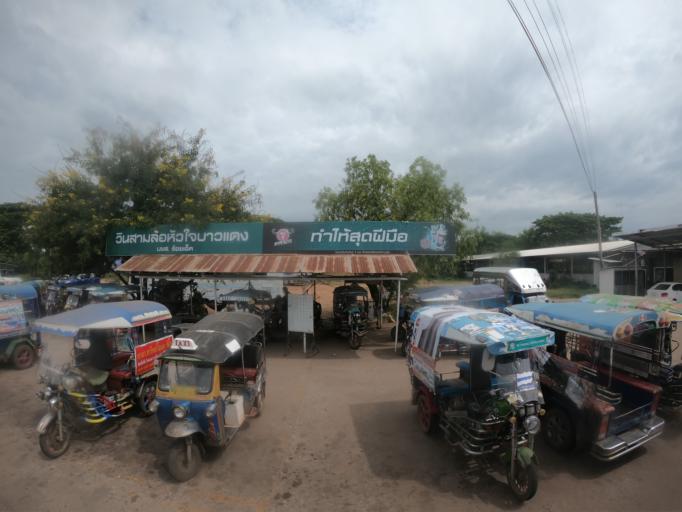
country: TH
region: Roi Et
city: Roi Et
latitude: 16.0535
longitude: 103.6402
